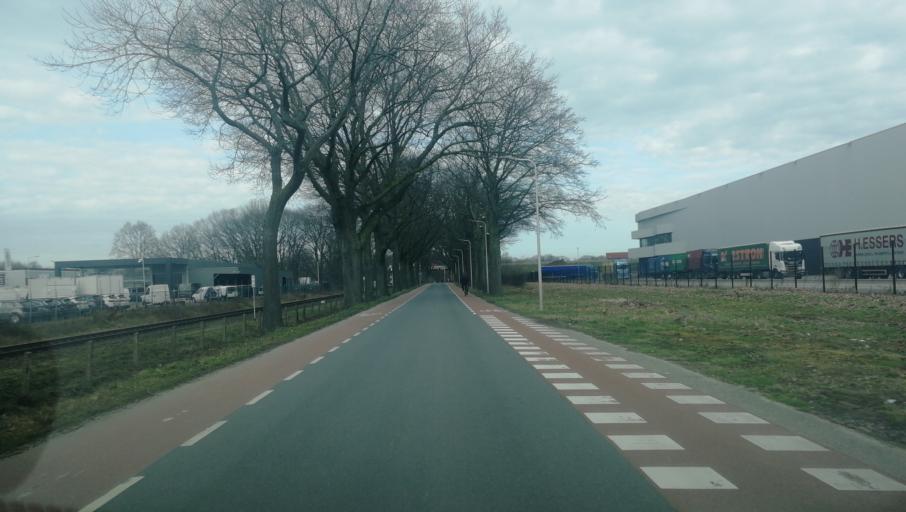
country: NL
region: Limburg
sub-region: Gemeente Venlo
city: Venlo
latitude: 51.3913
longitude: 6.1420
